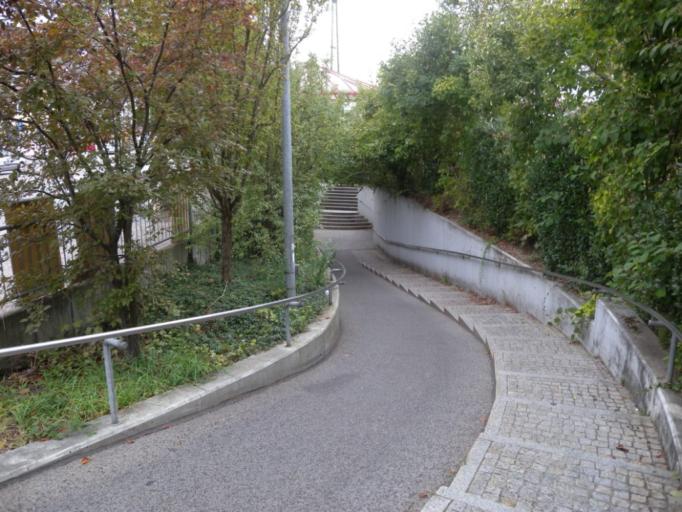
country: DE
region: Baden-Wuerttemberg
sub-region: Regierungsbezirk Stuttgart
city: Schorndorf
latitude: 48.8072
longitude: 9.5280
